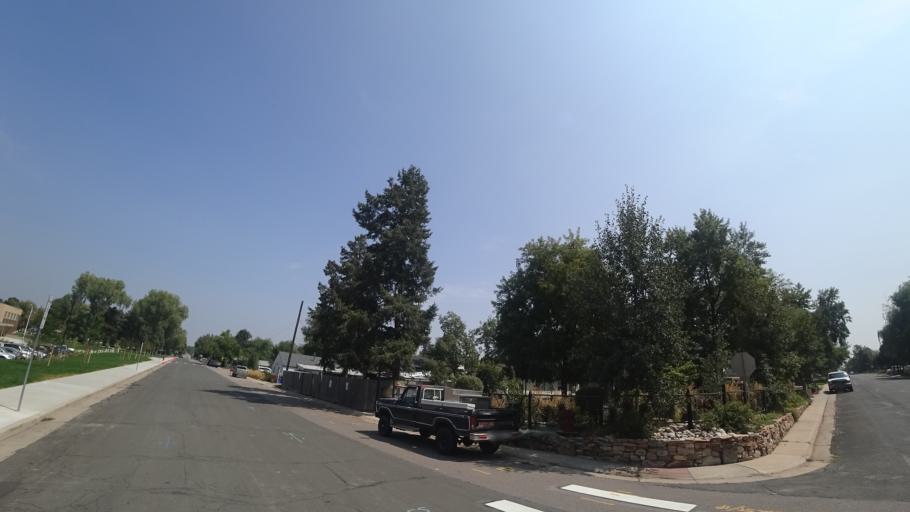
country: US
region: Colorado
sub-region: Arapahoe County
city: Englewood
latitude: 39.6314
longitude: -104.9948
